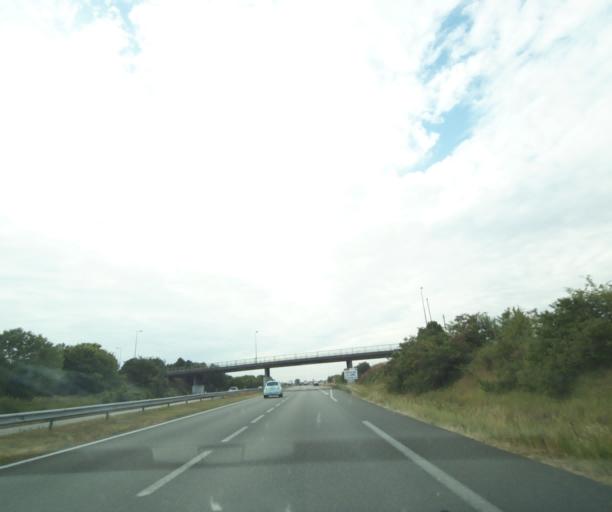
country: FR
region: Poitou-Charentes
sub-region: Departement de la Charente-Maritime
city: Angoulins
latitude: 46.1034
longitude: -1.0949
